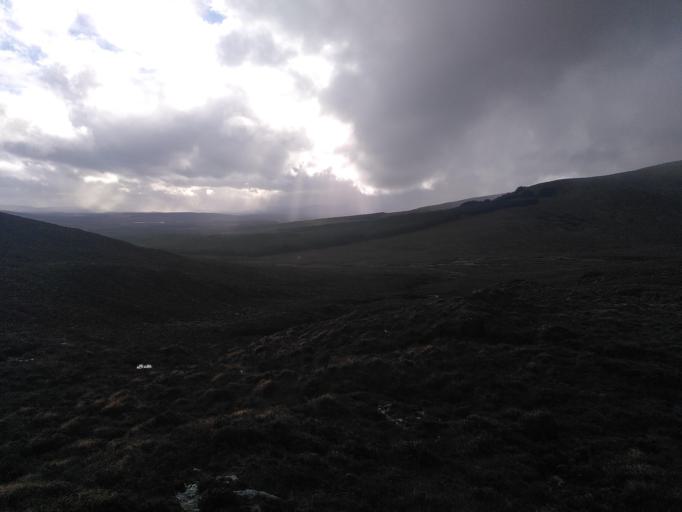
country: IE
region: Connaught
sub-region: Maigh Eo
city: Crossmolina
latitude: 53.9775
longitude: -9.4412
